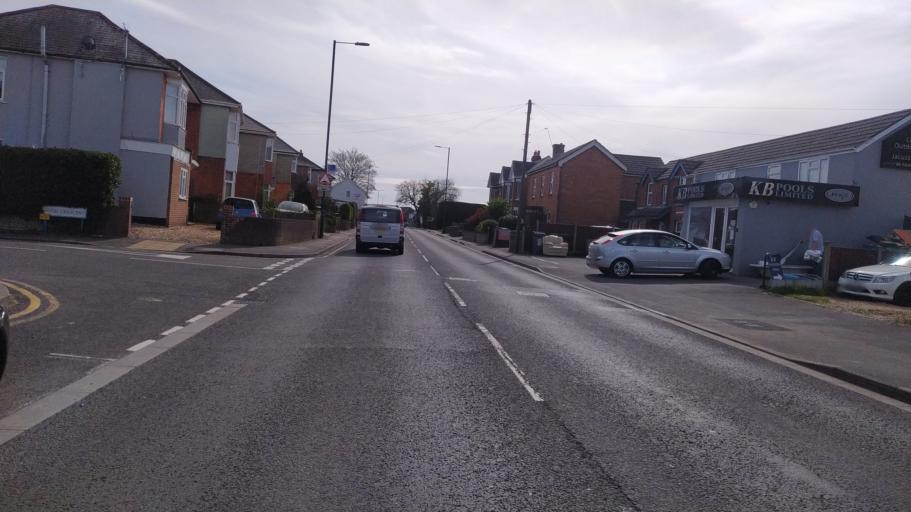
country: GB
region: England
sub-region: Bournemouth
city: Bournemouth
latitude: 50.7485
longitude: -1.9088
